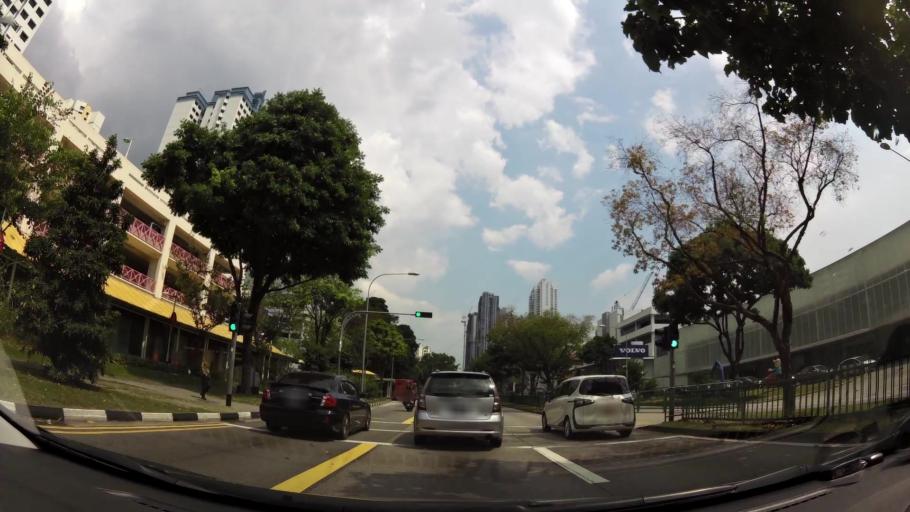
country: SG
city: Singapore
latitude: 1.2923
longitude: 103.8108
